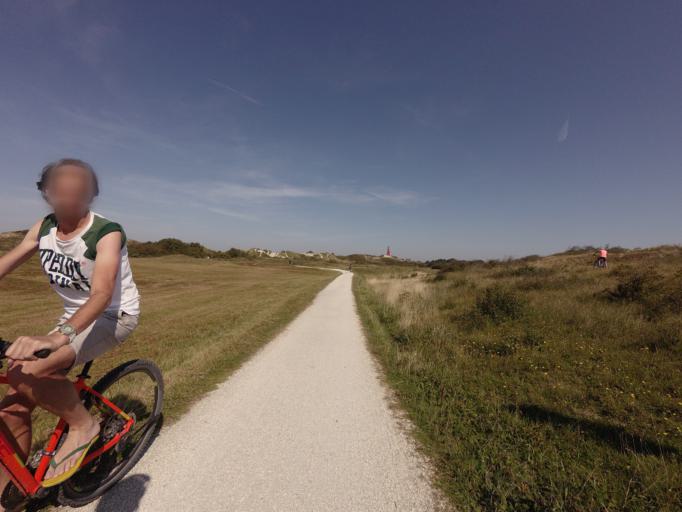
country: NL
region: Friesland
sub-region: Gemeente Schiermonnikoog
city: Schiermonnikoog
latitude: 53.4810
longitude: 6.1469
